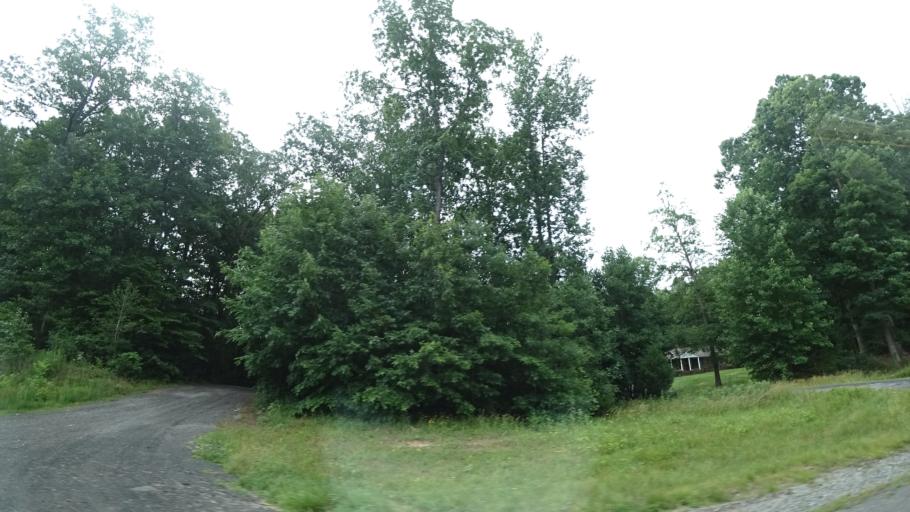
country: US
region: Virginia
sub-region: Spotsylvania County
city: Spotsylvania
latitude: 38.1979
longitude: -77.6112
